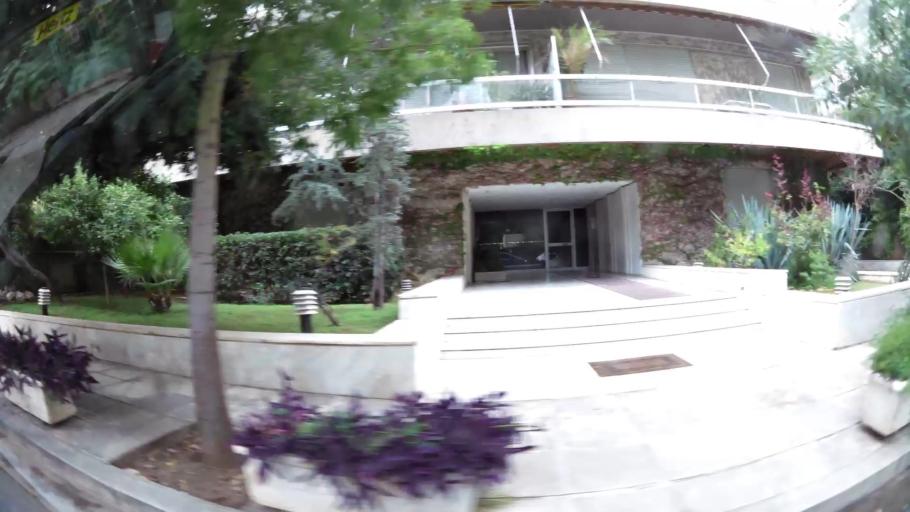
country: GR
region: Attica
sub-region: Nomarchia Athinas
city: Palaio Faliro
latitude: 37.9250
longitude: 23.6966
